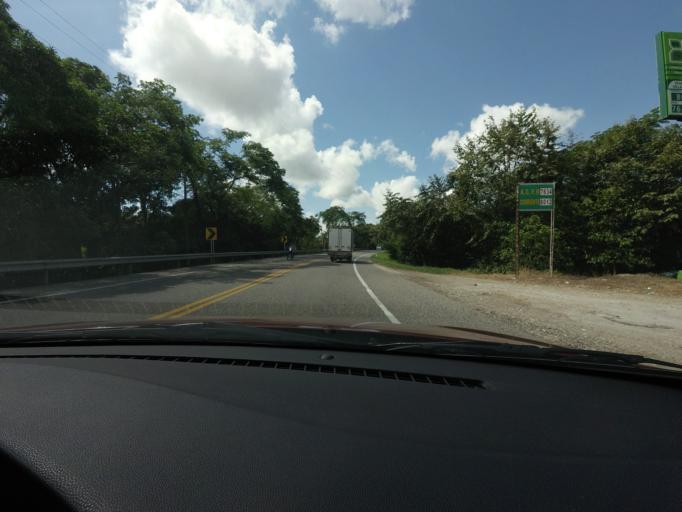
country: CO
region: Tolima
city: Saldana
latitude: 3.9418
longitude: -75.0125
